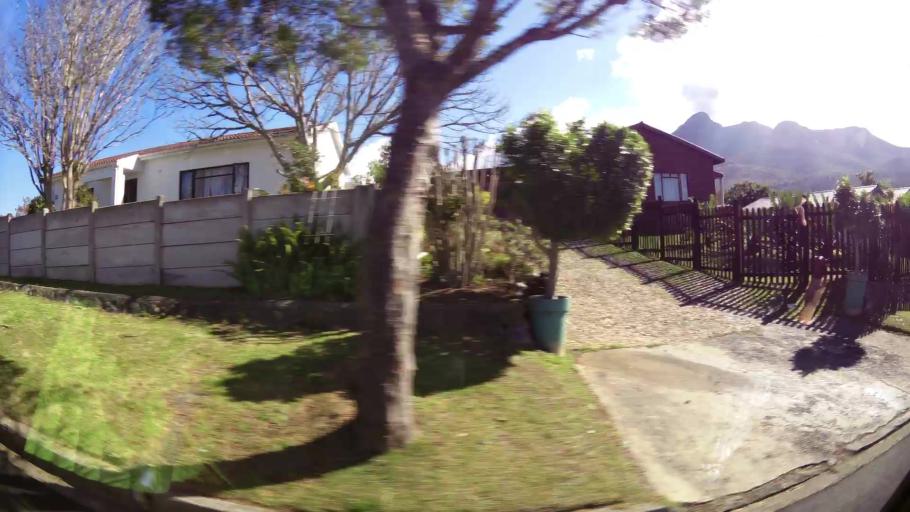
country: ZA
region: Western Cape
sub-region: Eden District Municipality
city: George
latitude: -33.9473
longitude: 22.4762
